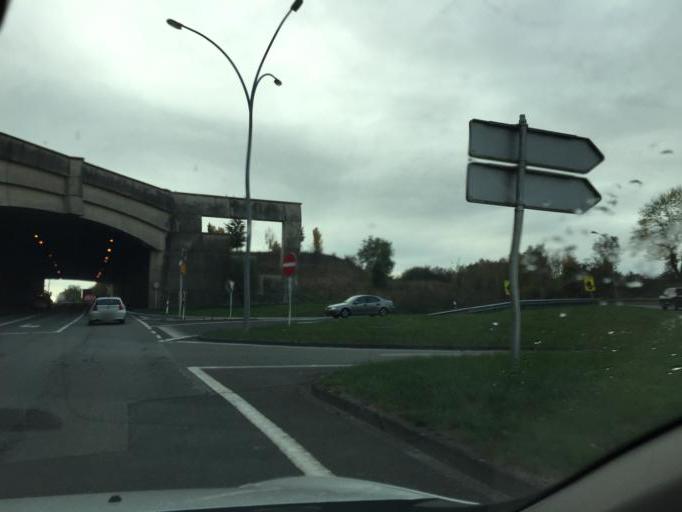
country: LU
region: Luxembourg
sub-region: Canton de Mersch
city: Mersch
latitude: 49.7637
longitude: 6.0901
